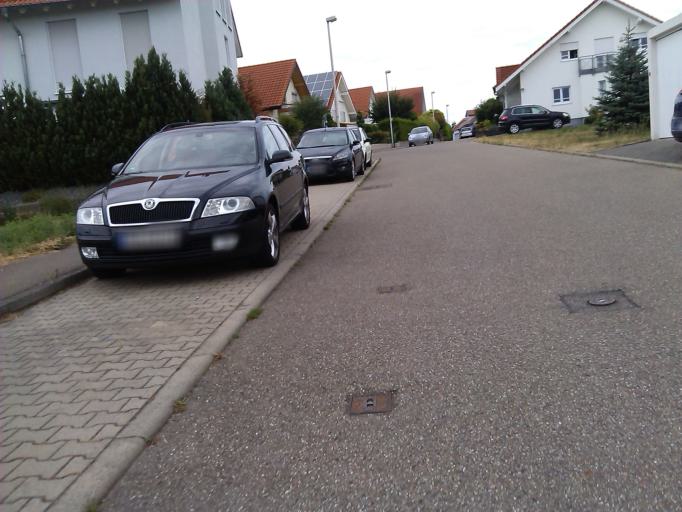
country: DE
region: Baden-Wuerttemberg
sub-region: Regierungsbezirk Stuttgart
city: Talheim
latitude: 49.0769
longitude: 9.1911
